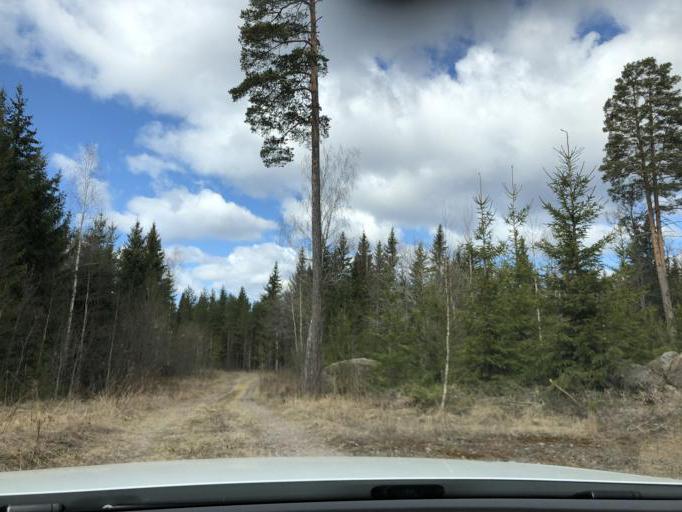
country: SE
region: Uppsala
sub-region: Tierps Kommun
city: Tierp
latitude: 60.3323
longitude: 17.3352
